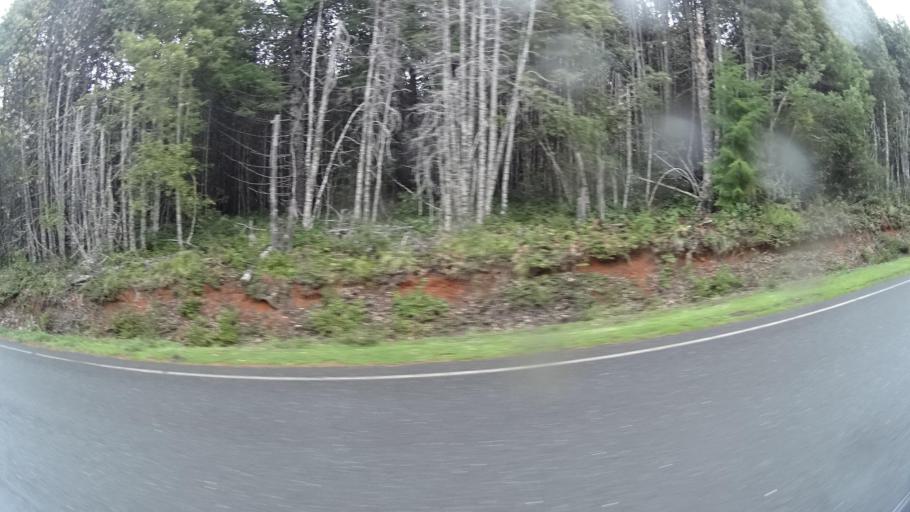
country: US
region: California
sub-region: Humboldt County
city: Willow Creek
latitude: 41.1899
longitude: -123.8154
